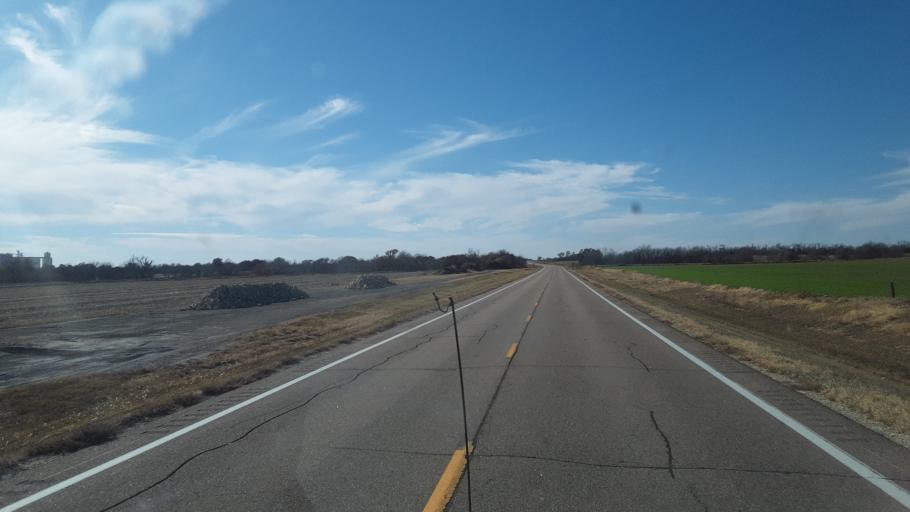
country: US
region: Kansas
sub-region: Pawnee County
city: Larned
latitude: 38.1896
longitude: -99.2966
